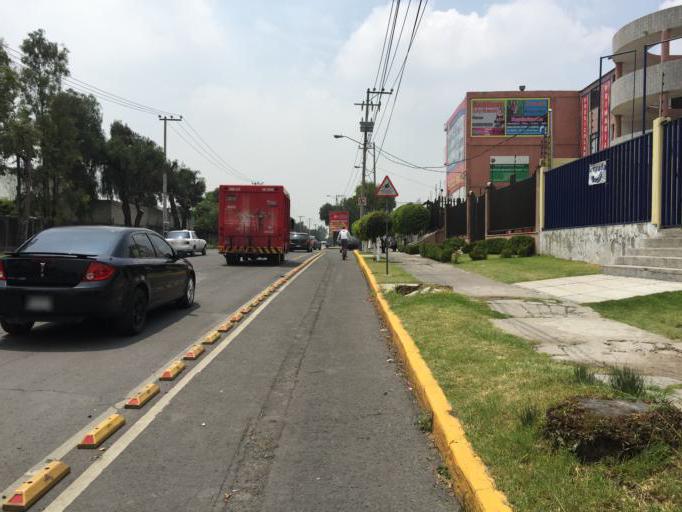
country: MX
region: Mexico
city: Cuautitlan Izcalli
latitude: 19.6417
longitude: -99.2037
